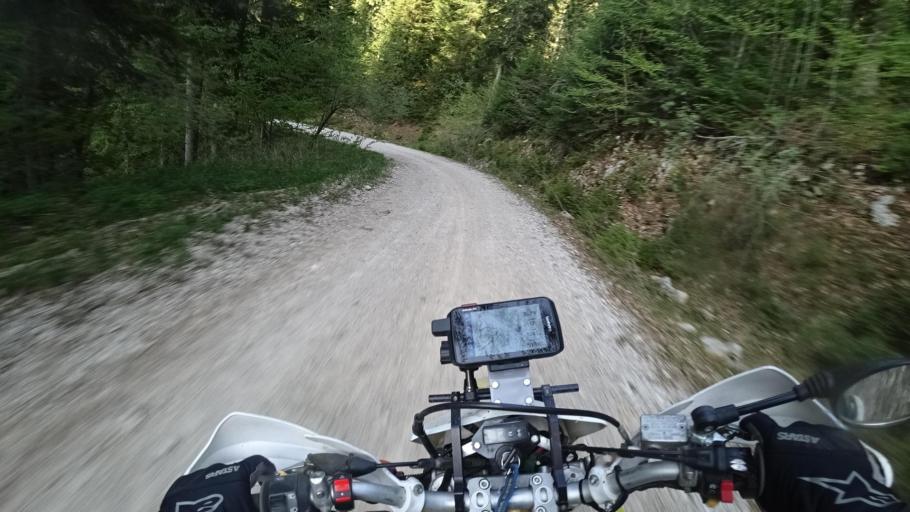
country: BA
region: Federation of Bosnia and Herzegovina
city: Rumboci
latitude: 43.7253
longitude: 17.5288
